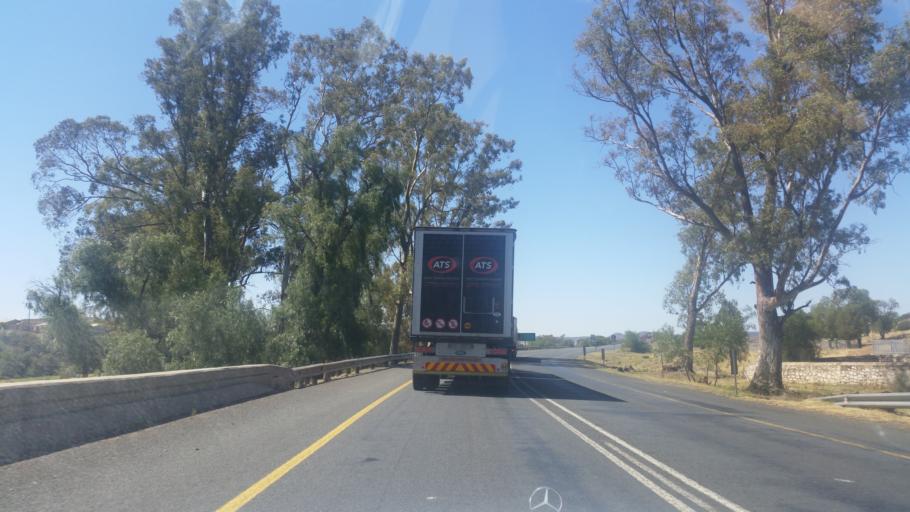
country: ZA
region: Northern Cape
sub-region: Pixley ka Seme District Municipality
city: Colesberg
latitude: -30.7120
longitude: 25.1007
